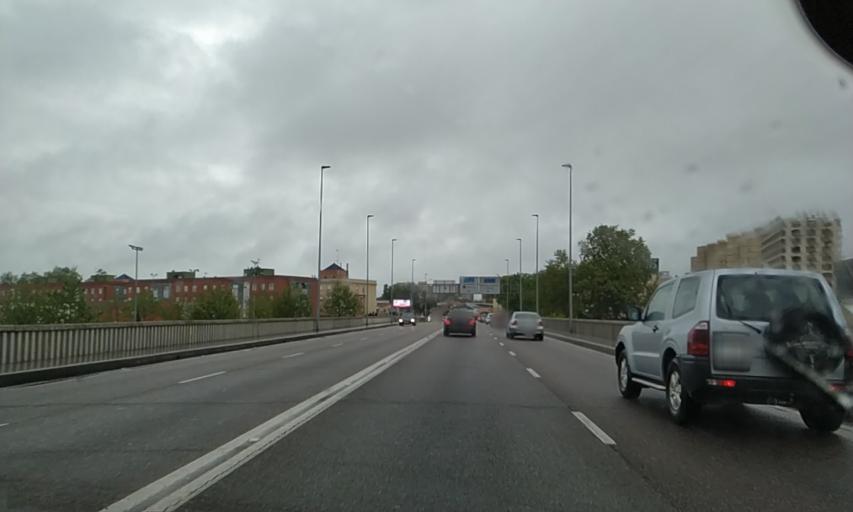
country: ES
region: Extremadura
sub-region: Provincia de Badajoz
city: Badajoz
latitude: 38.8820
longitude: -6.9838
